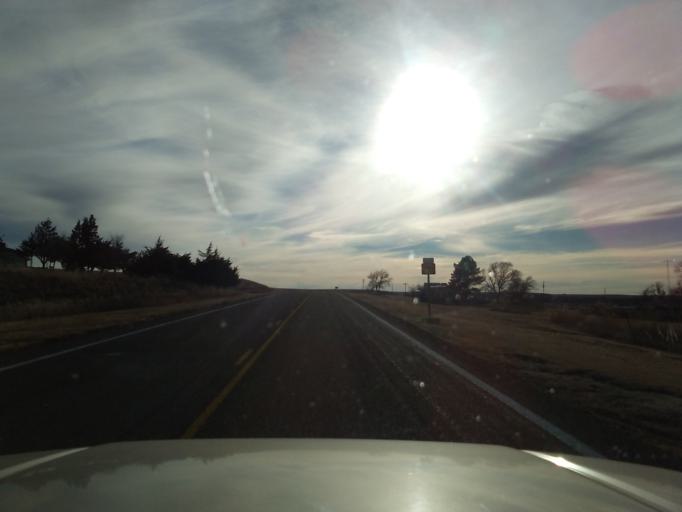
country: US
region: Kansas
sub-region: Norton County
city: Norton
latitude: 39.7361
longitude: -100.1748
